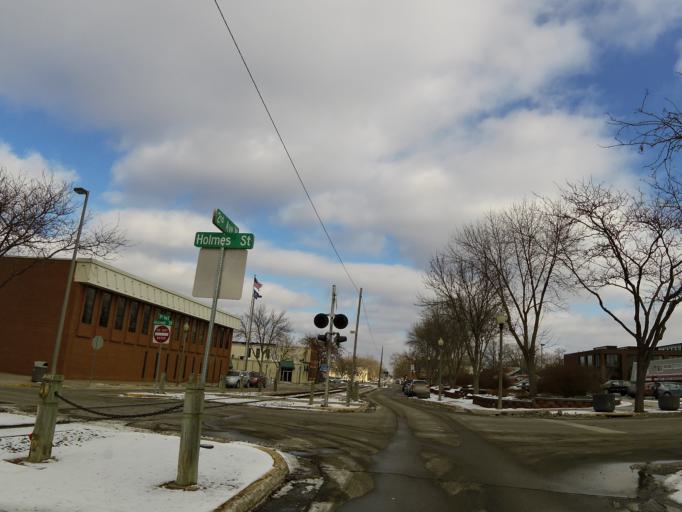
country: US
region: Minnesota
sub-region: Scott County
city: Shakopee
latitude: 44.7975
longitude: -93.5267
